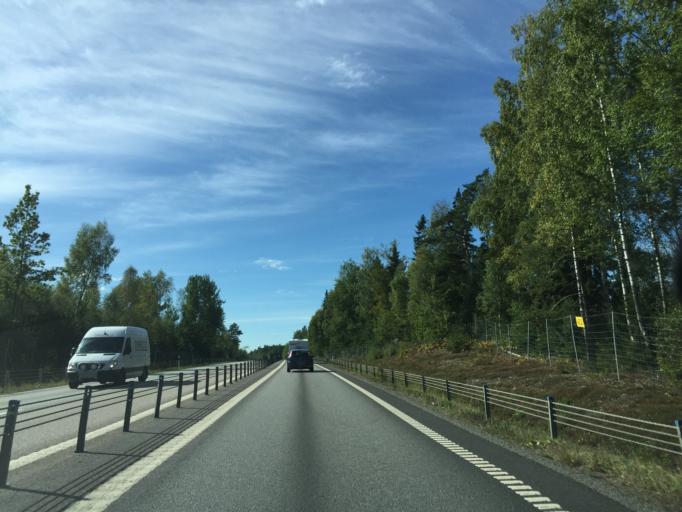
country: SE
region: Vaestmanland
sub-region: Hallstahammars Kommun
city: Hallstahammar
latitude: 59.5824
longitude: 16.1607
